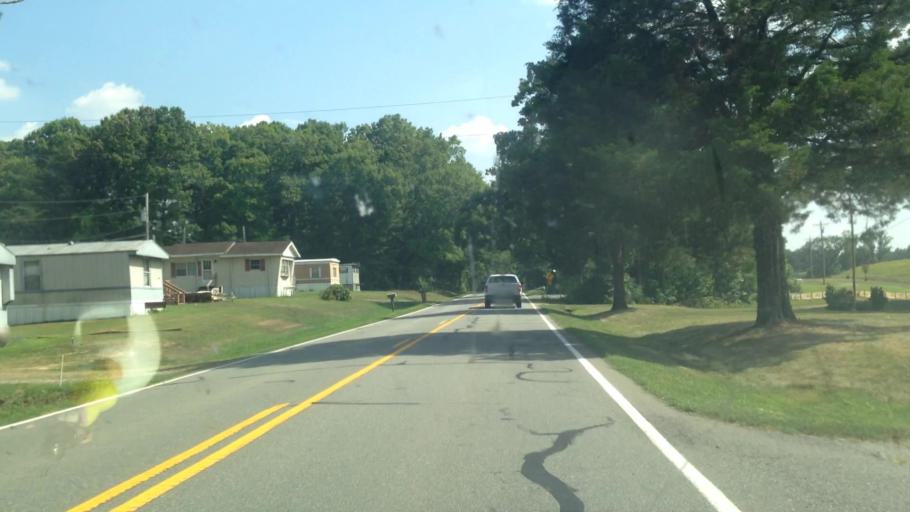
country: US
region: North Carolina
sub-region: Stokes County
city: Walnut Cove
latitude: 36.2731
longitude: -80.0883
